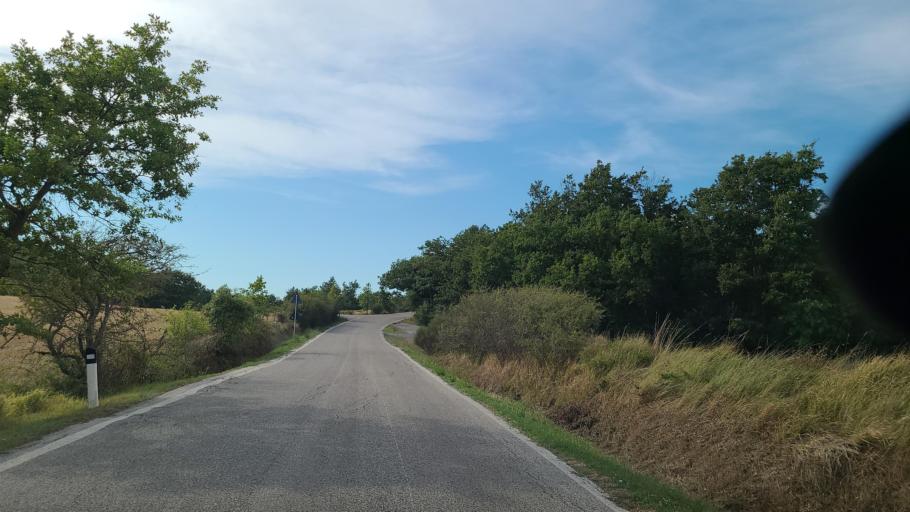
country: IT
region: Tuscany
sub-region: Provincia di Siena
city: San Gimignano
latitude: 43.4293
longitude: 10.9699
